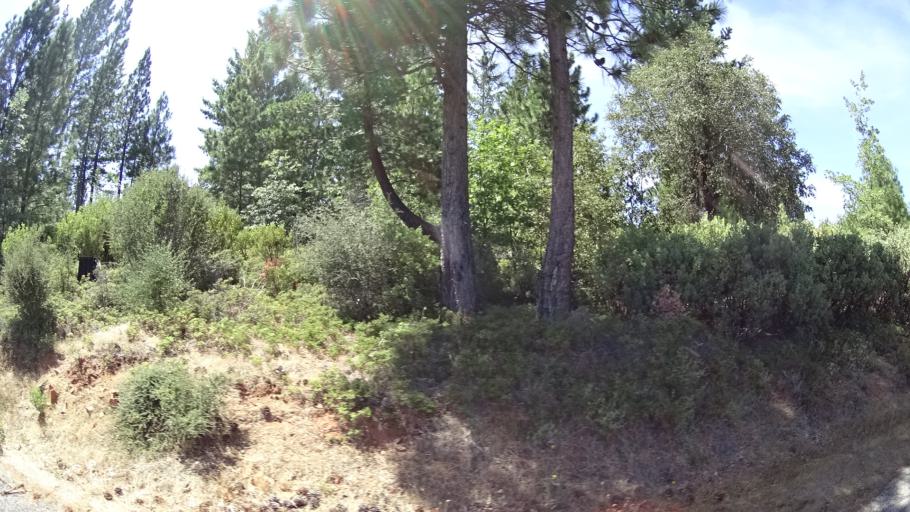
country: US
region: California
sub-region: Calaveras County
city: Forest Meadows
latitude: 38.1913
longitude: -120.4075
